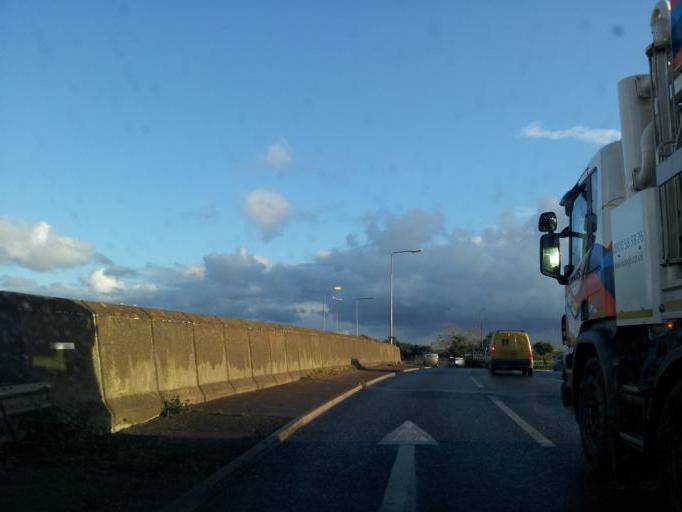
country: GB
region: England
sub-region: Norfolk
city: Great Yarmouth
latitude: 52.6150
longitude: 1.7182
